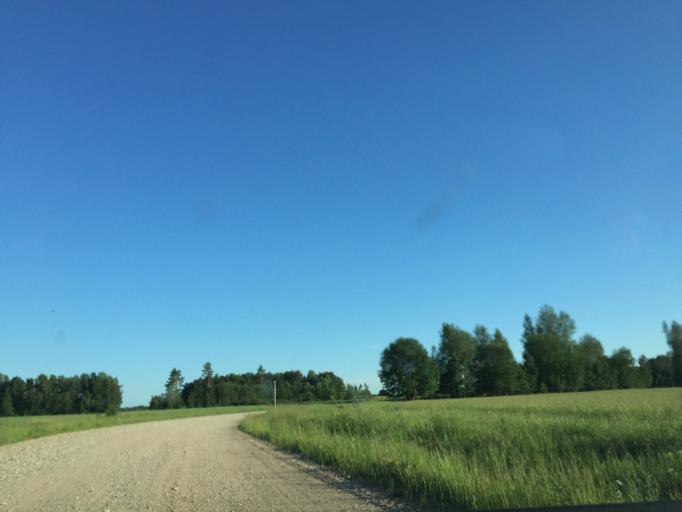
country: LV
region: Broceni
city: Broceni
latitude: 56.8396
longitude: 22.5663
